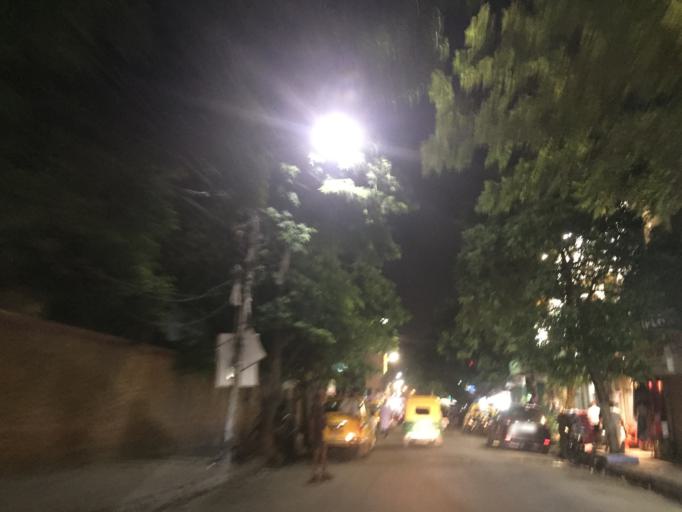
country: IN
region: West Bengal
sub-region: Kolkata
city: Kolkata
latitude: 22.5585
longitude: 88.3549
